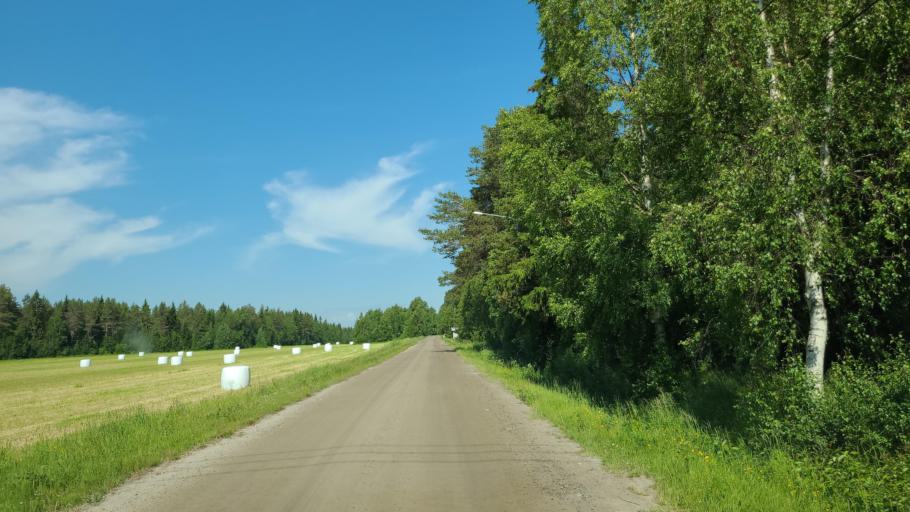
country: SE
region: Vaesterbotten
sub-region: Robertsfors Kommun
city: Robertsfors
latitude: 64.0826
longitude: 20.8465
